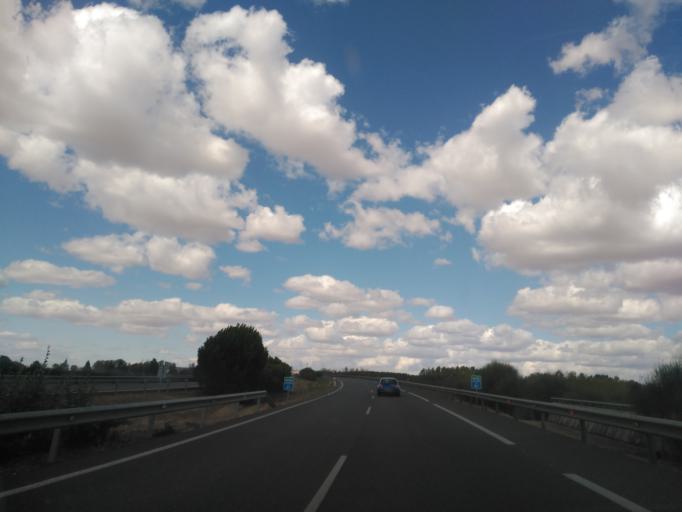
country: ES
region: Castille and Leon
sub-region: Provincia de Palencia
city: Venta de Banos
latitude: 41.9272
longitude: -4.4996
